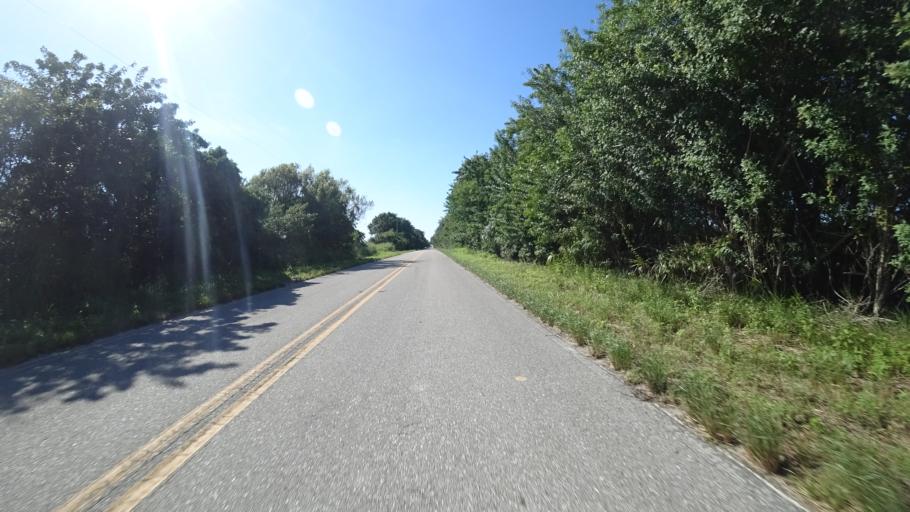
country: US
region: Florida
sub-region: Hillsborough County
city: Wimauma
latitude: 27.6309
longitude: -82.2925
